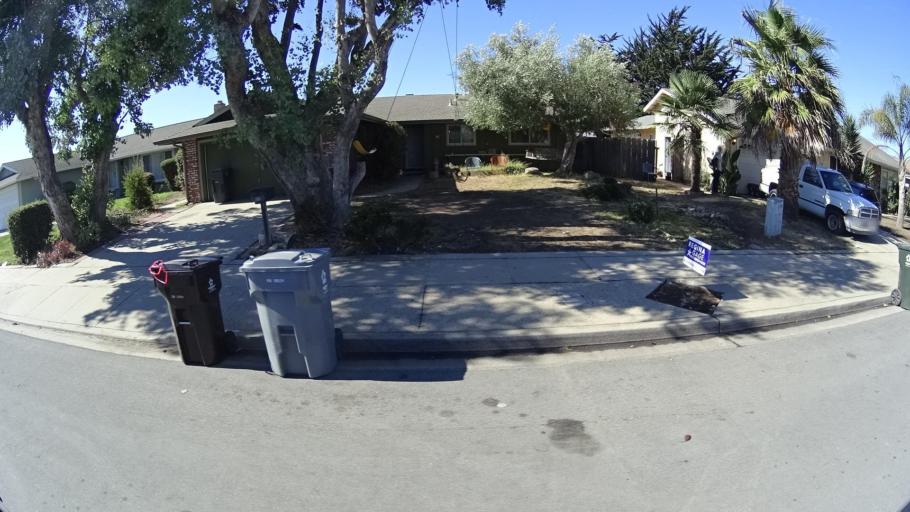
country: US
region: California
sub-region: Monterey County
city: Boronda
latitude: 36.6928
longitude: -121.6661
